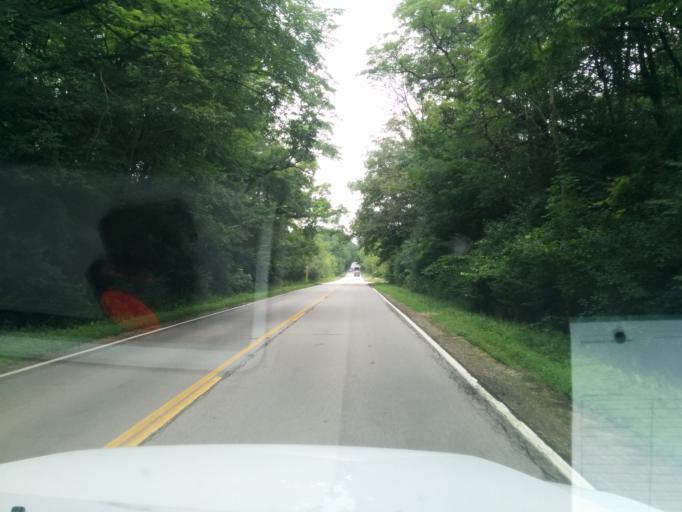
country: US
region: Illinois
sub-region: Cook County
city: Willow Springs
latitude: 41.7090
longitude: -87.8756
